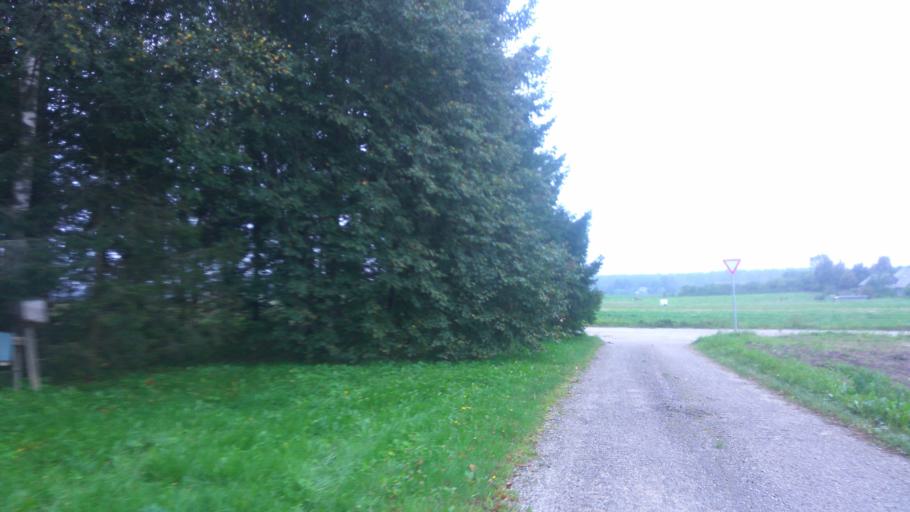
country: LV
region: Rucavas
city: Rucava
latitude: 56.1537
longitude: 21.1716
